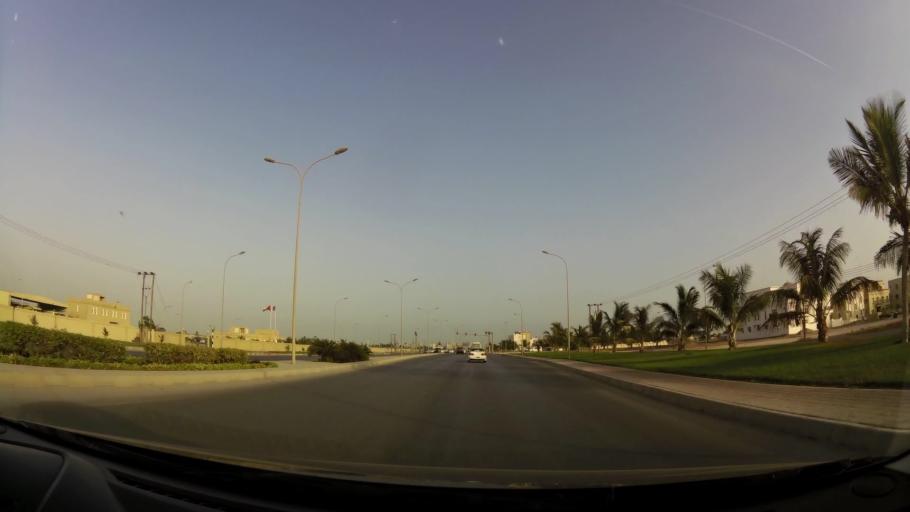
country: OM
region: Zufar
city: Salalah
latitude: 17.0140
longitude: 54.0363
